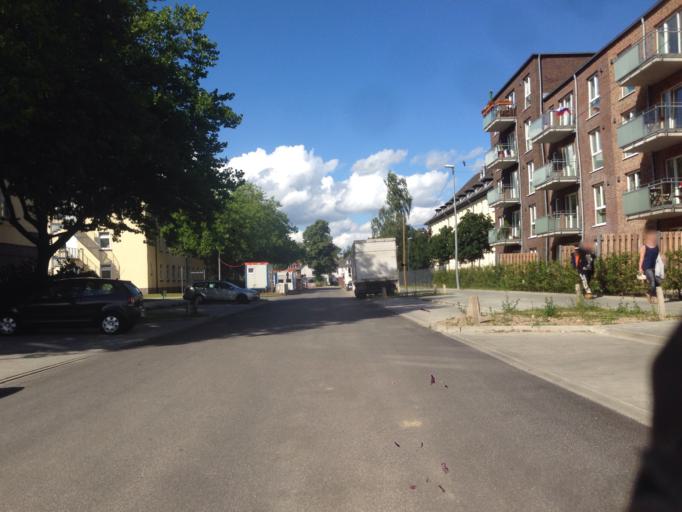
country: DE
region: Hamburg
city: Farmsen-Berne
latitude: 53.5825
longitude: 10.1327
